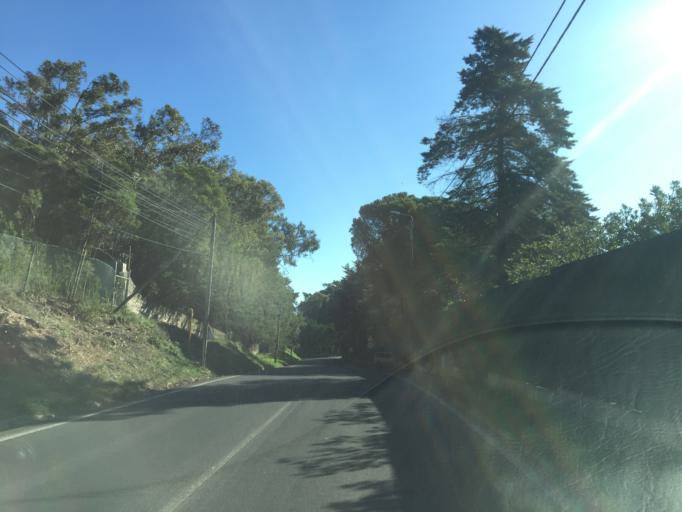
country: PT
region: Lisbon
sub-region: Sintra
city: Belas
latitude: 38.7992
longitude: -9.2734
